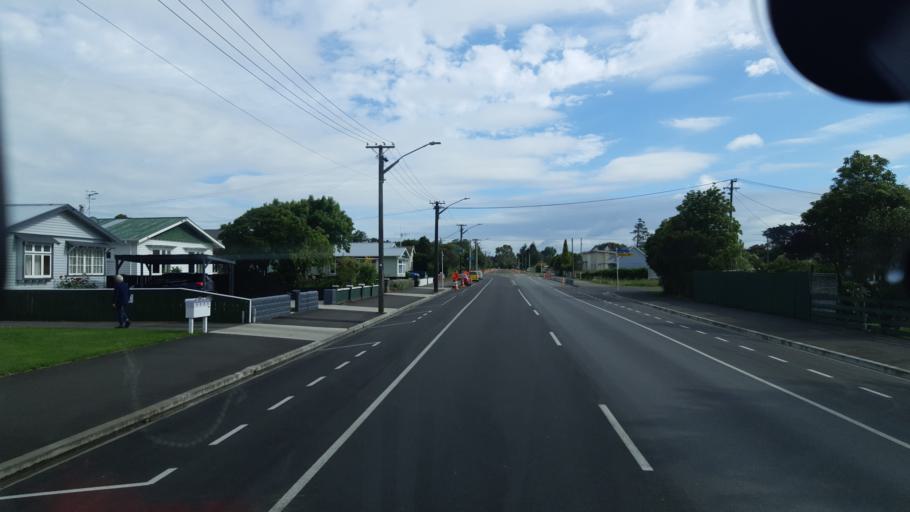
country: NZ
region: Manawatu-Wanganui
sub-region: Rangitikei District
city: Bulls
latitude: -40.0645
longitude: 175.3794
